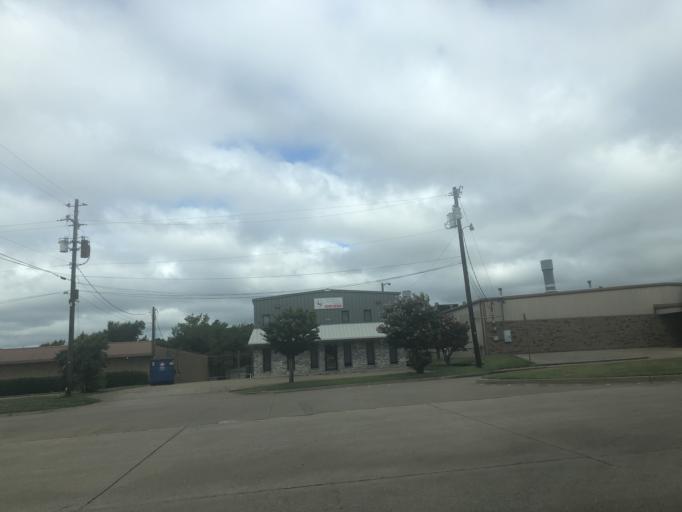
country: US
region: Texas
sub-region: Dallas County
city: Duncanville
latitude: 32.6383
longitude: -96.9240
